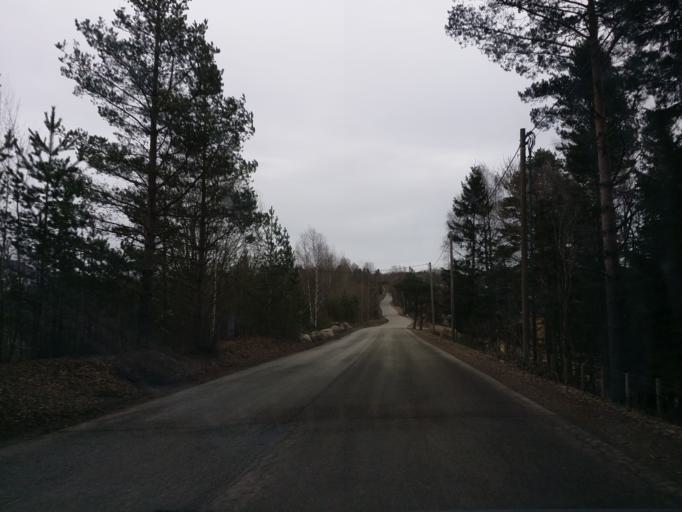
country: NO
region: Buskerud
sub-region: Lier
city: Tranby
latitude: 59.8159
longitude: 10.2392
